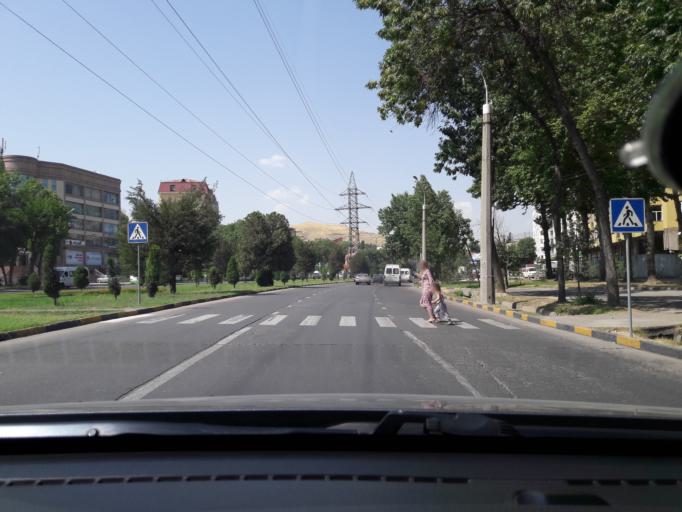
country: TJ
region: Dushanbe
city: Dushanbe
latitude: 38.5885
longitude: 68.7412
